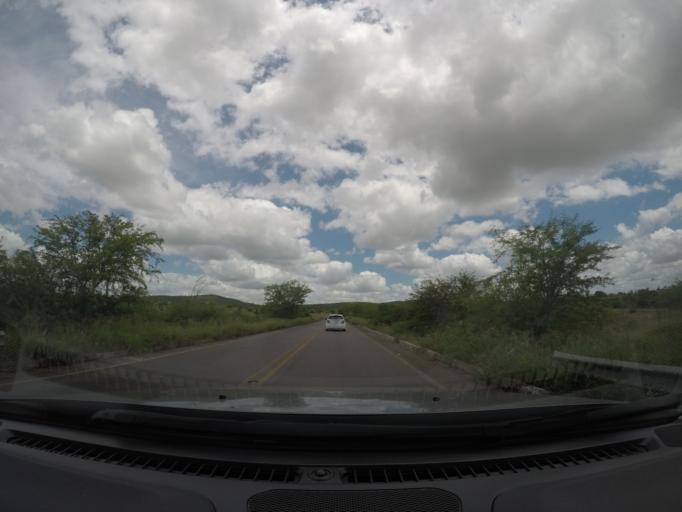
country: BR
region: Bahia
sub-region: Ipira
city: Ipira
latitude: -12.2715
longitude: -39.8413
